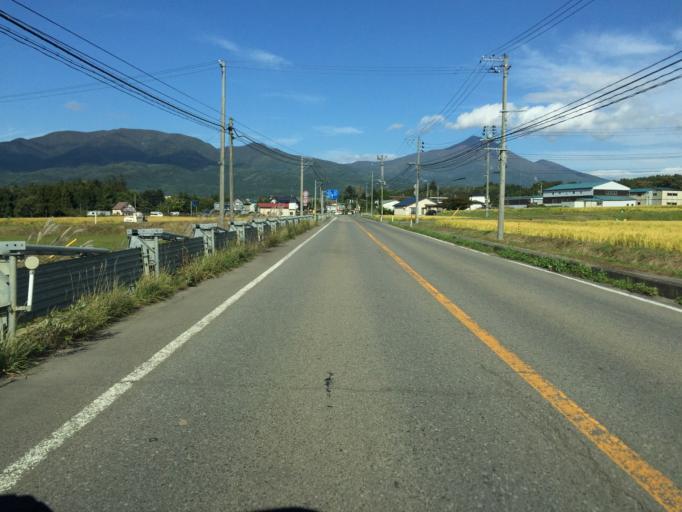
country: JP
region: Fukushima
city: Kitakata
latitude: 37.5336
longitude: 139.9610
